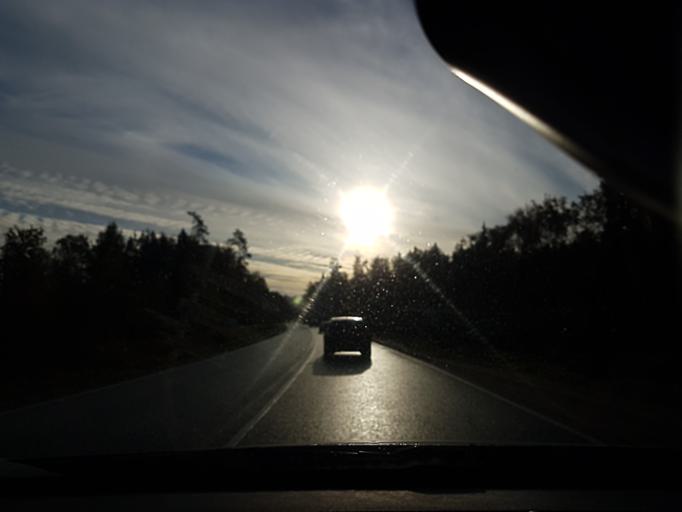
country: RU
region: Moskovskaya
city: Rozhdestveno
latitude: 55.8332
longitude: 37.0210
